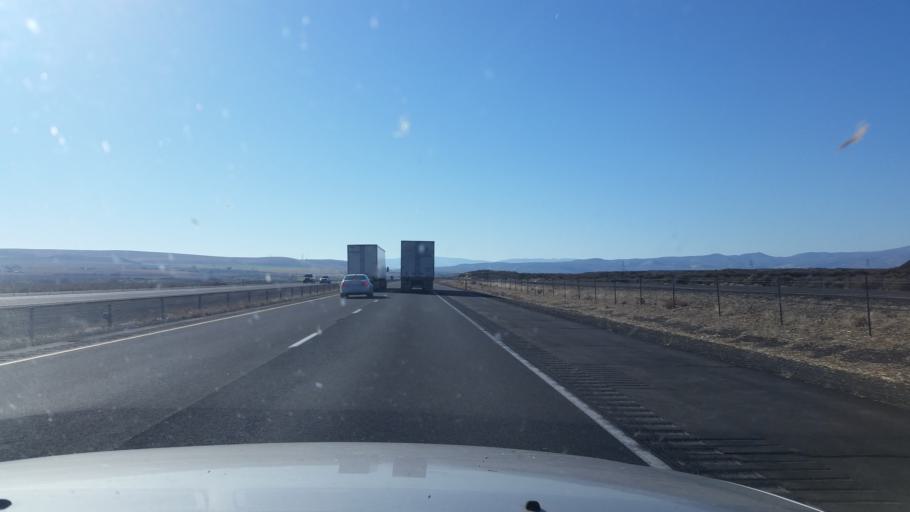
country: US
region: Washington
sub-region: Grant County
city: Quincy
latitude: 47.0432
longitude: -119.9168
